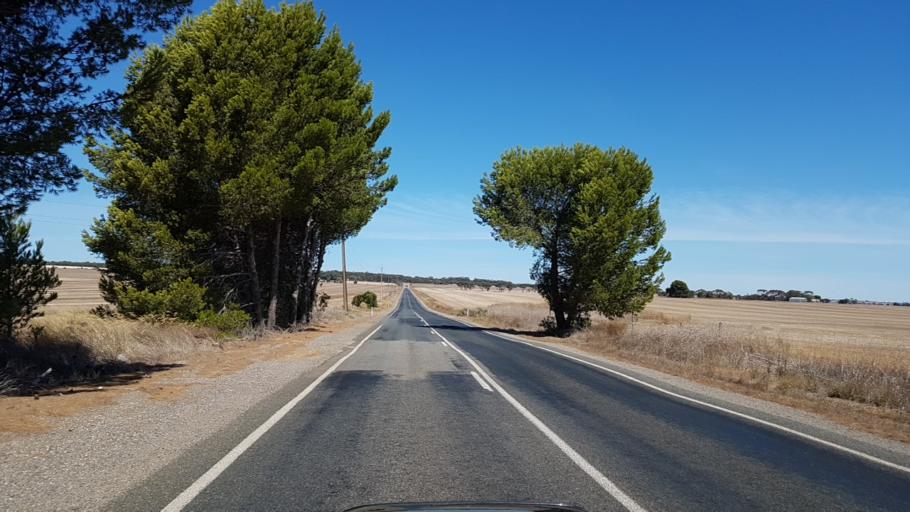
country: AU
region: South Australia
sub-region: Yorke Peninsula
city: Maitland
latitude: -34.3519
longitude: 137.6628
